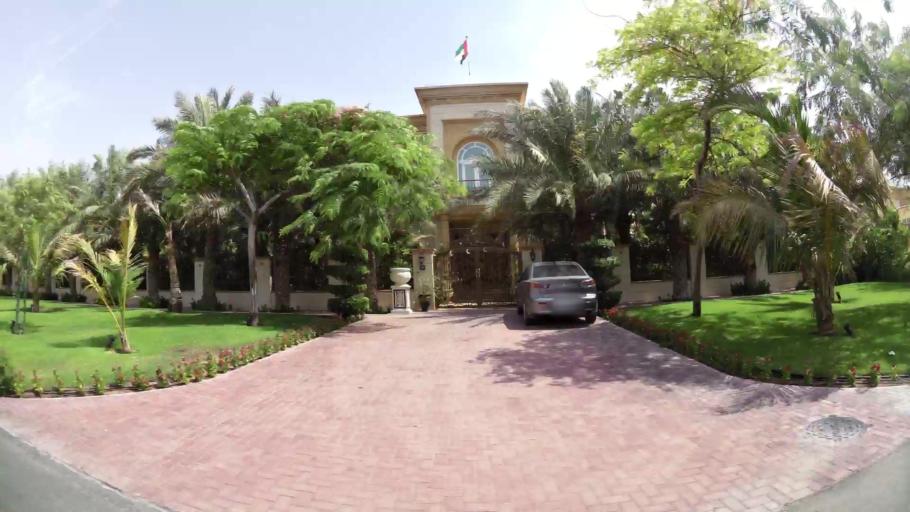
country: AE
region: Ash Shariqah
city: Sharjah
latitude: 25.2481
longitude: 55.4267
